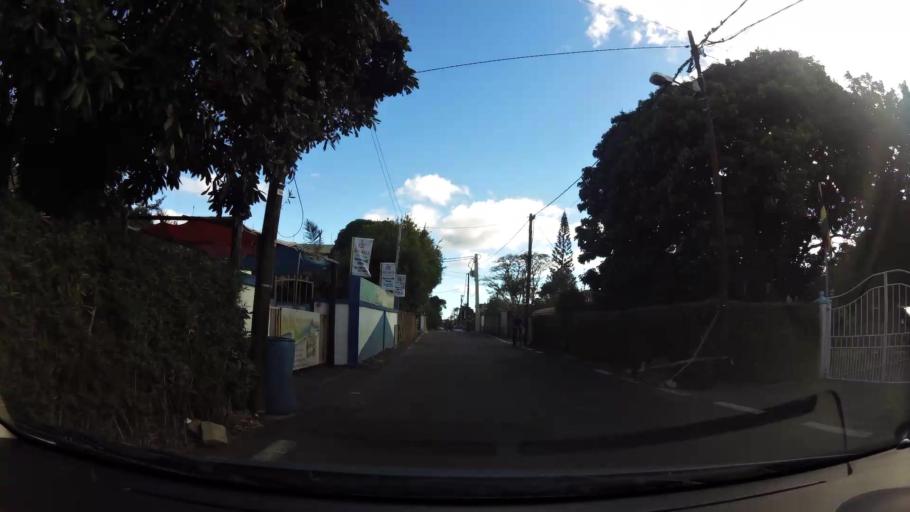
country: MU
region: Plaines Wilhems
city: Vacoas
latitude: -20.2967
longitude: 57.4882
